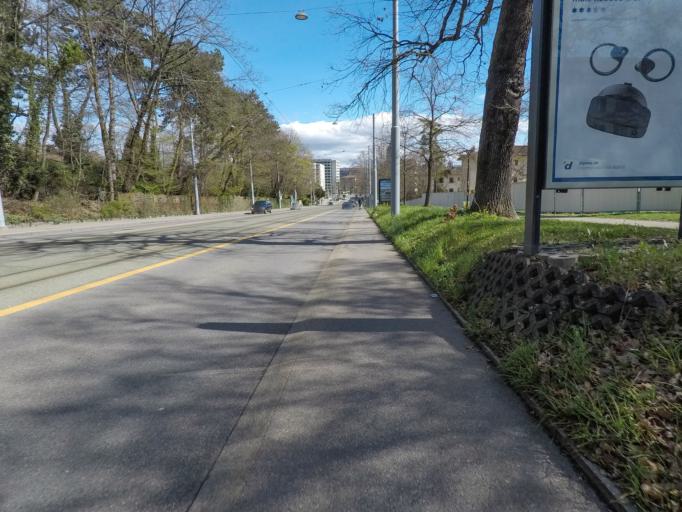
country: CH
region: Geneva
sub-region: Geneva
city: Le Grand-Saconnex
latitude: 46.2156
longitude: 6.1220
